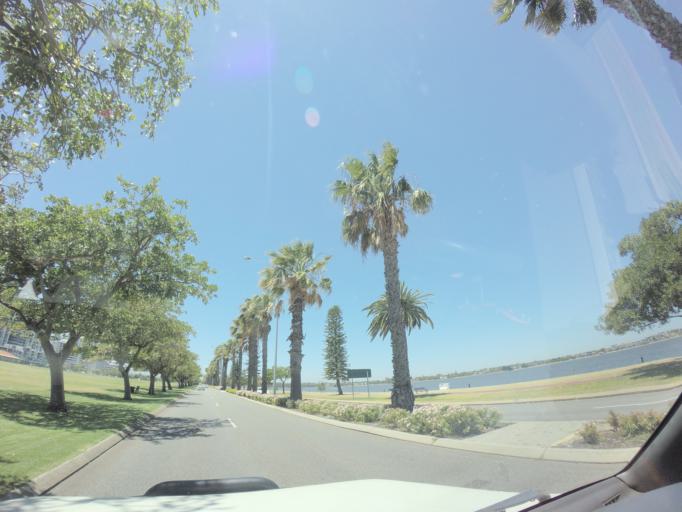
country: AU
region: Western Australia
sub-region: City of Perth
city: East Perth
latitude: -31.9610
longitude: 115.8656
